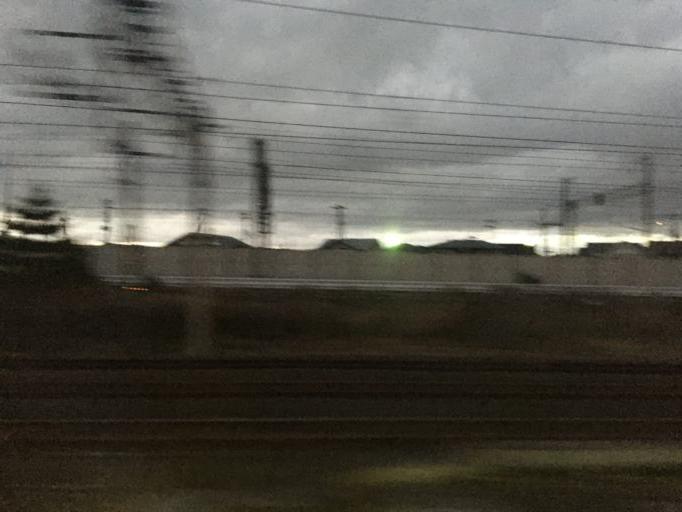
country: JP
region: Aomori
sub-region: Hachinohe Shi
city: Uchimaru
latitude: 40.5141
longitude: 141.4362
